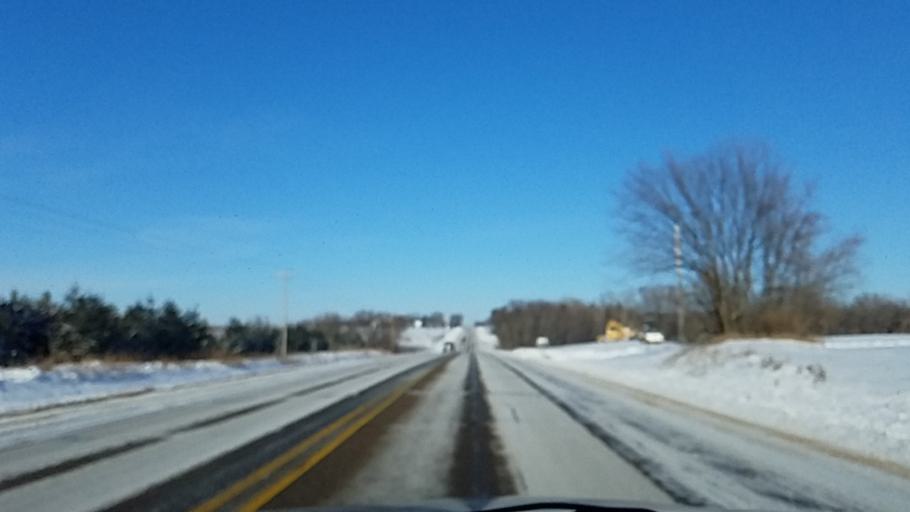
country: US
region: Wisconsin
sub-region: Saint Croix County
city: New Richmond
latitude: 45.0545
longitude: -92.5373
